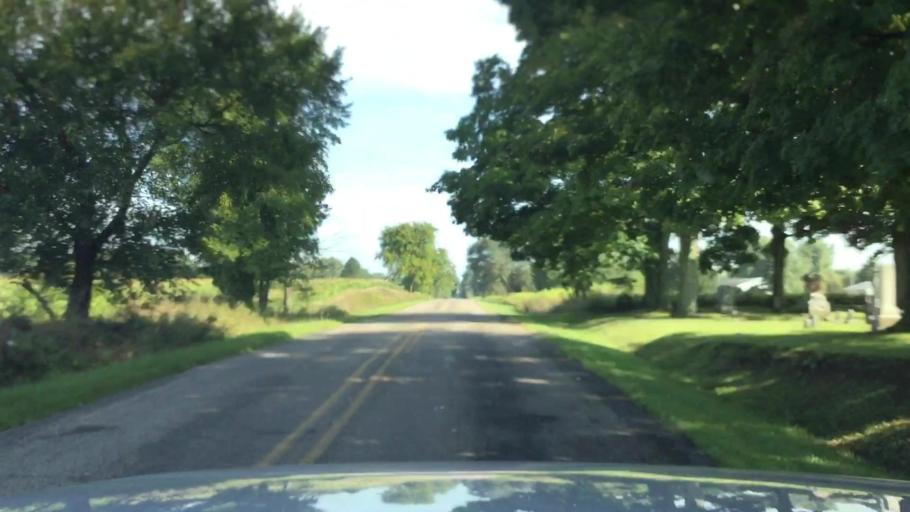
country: US
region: Michigan
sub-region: Lenawee County
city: Hudson
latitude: 41.8859
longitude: -84.4202
